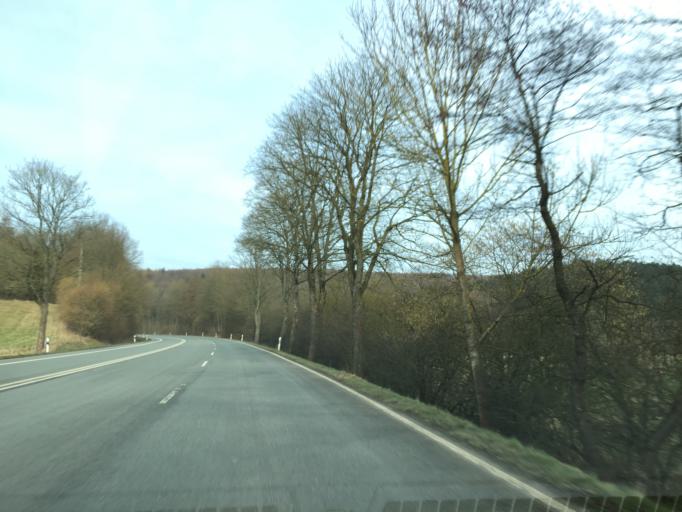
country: DE
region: North Rhine-Westphalia
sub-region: Regierungsbezirk Detmold
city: Willebadessen
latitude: 51.5509
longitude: 9.0143
